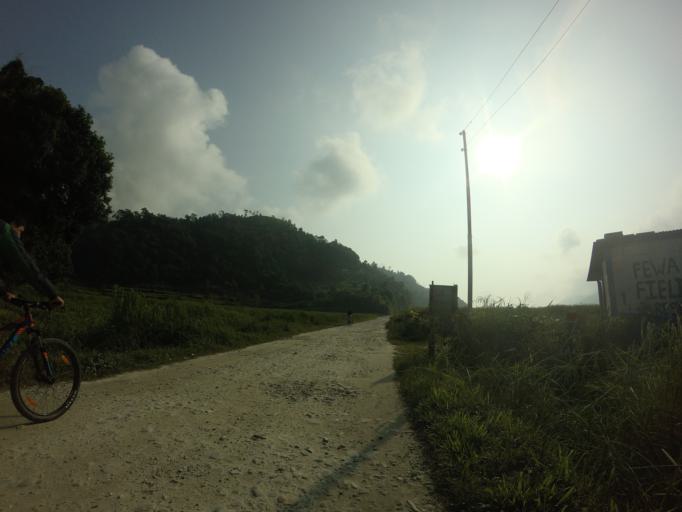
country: NP
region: Western Region
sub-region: Gandaki Zone
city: Pokhara
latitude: 28.2352
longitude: 83.9114
